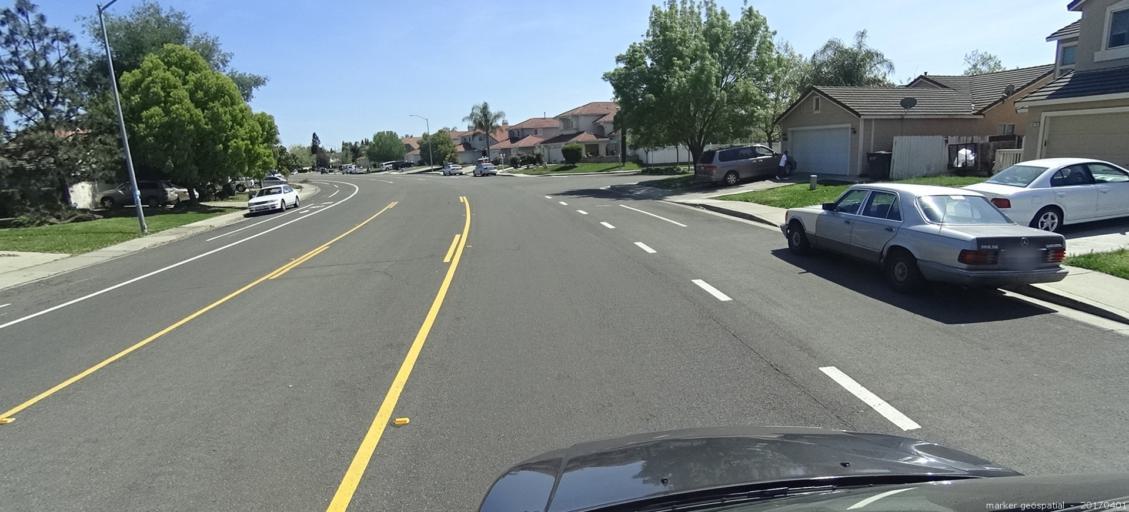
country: US
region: California
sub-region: Sacramento County
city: Laguna
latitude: 38.4468
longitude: -121.4406
